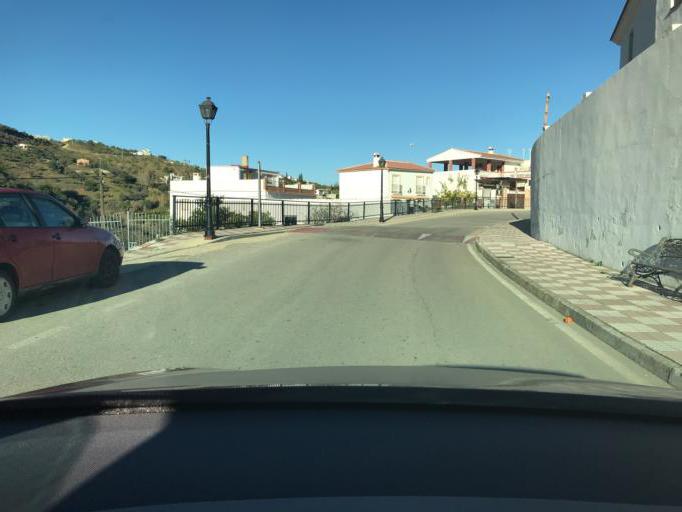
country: ES
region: Andalusia
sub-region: Provincia de Malaga
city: Tolox
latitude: 36.6880
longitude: -4.9012
